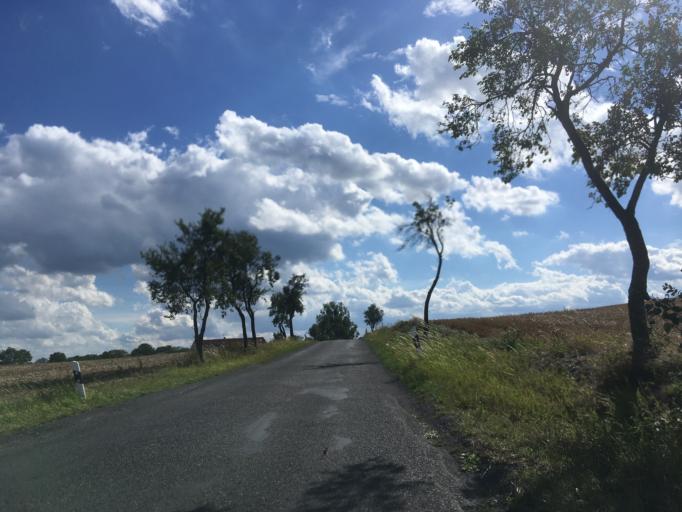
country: DE
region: Brandenburg
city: Angermunde
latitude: 52.9548
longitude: 14.0027
